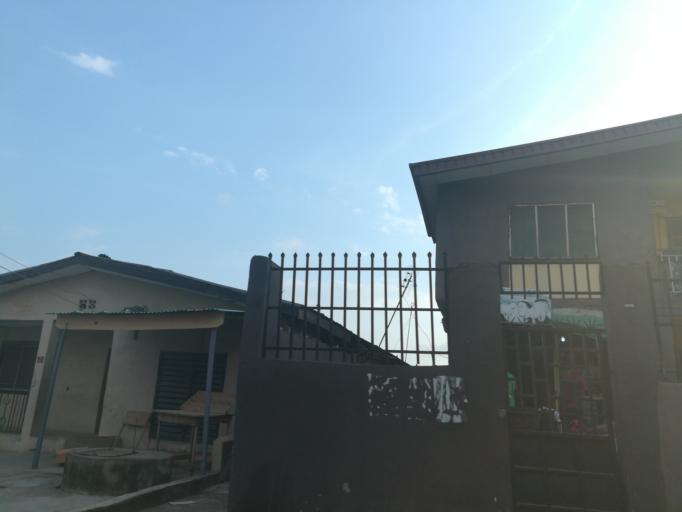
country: NG
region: Lagos
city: Ojota
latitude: 6.5916
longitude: 3.3964
